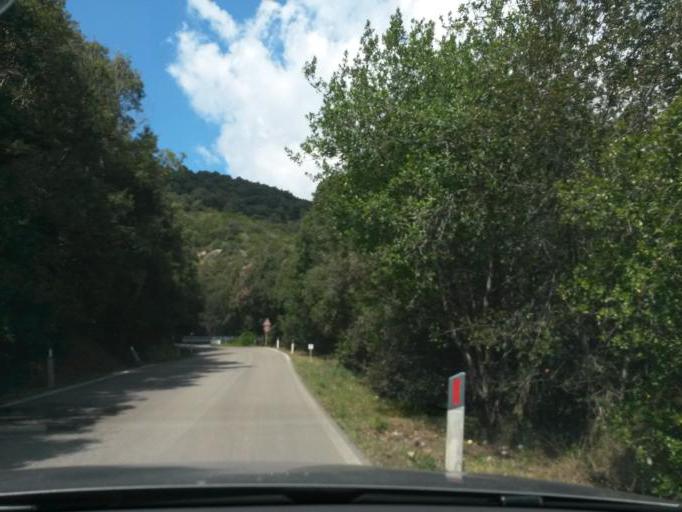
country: IT
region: Tuscany
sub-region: Provincia di Livorno
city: Campo nell'Elba
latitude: 42.7429
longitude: 10.2076
